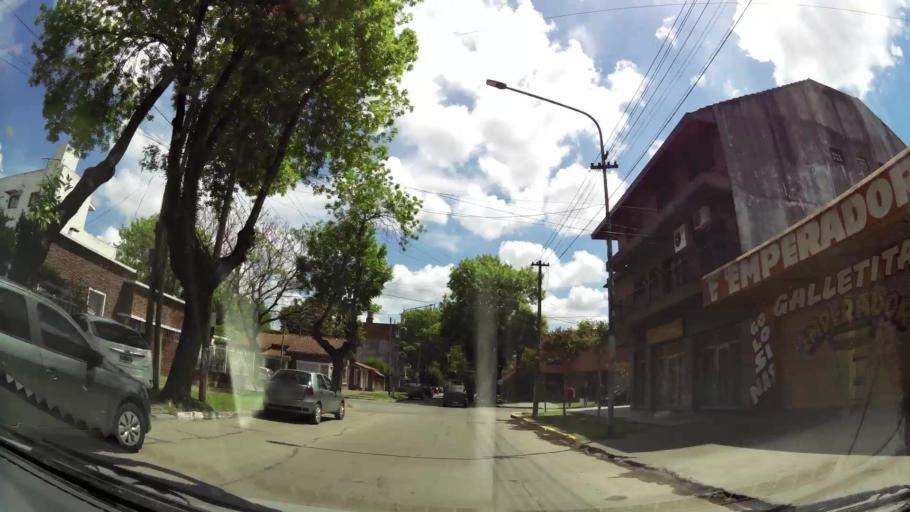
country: AR
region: Buenos Aires
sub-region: Partido de Quilmes
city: Quilmes
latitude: -34.8087
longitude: -58.2712
